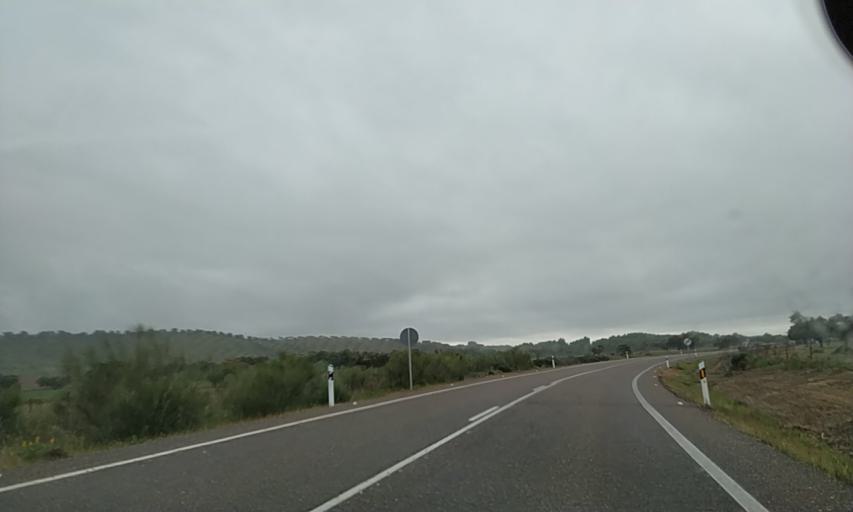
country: ES
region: Extremadura
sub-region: Provincia de Badajoz
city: La Roca de la Sierra
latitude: 39.0909
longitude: -6.7193
